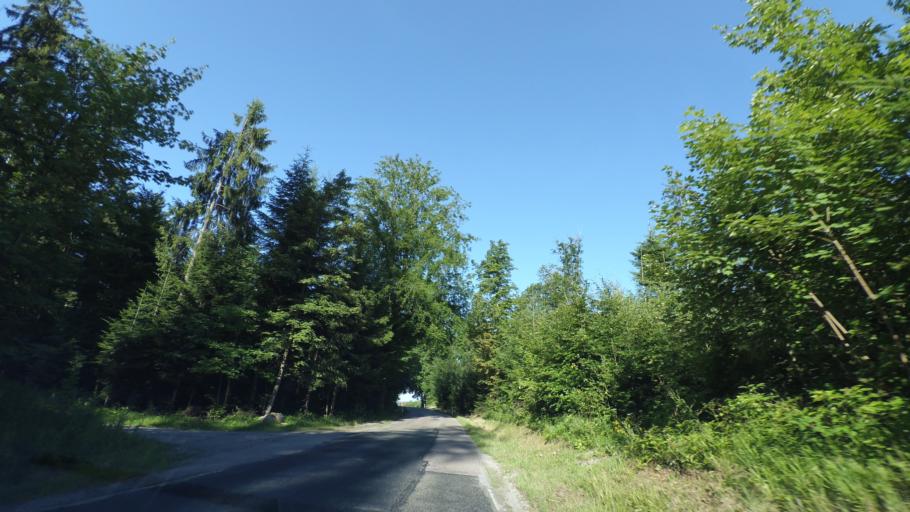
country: DE
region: Baden-Wuerttemberg
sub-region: Regierungsbezirk Stuttgart
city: Oberrot
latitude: 49.0150
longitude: 9.6226
